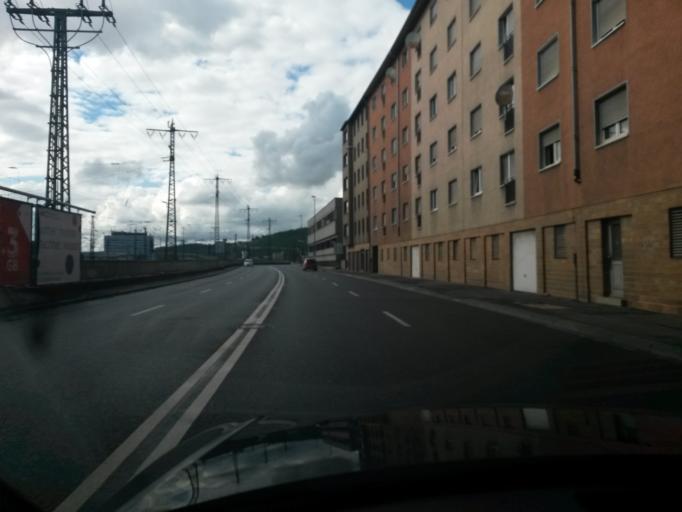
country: DE
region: Bavaria
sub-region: Regierungsbezirk Unterfranken
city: Wuerzburg
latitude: 49.8012
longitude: 9.9437
